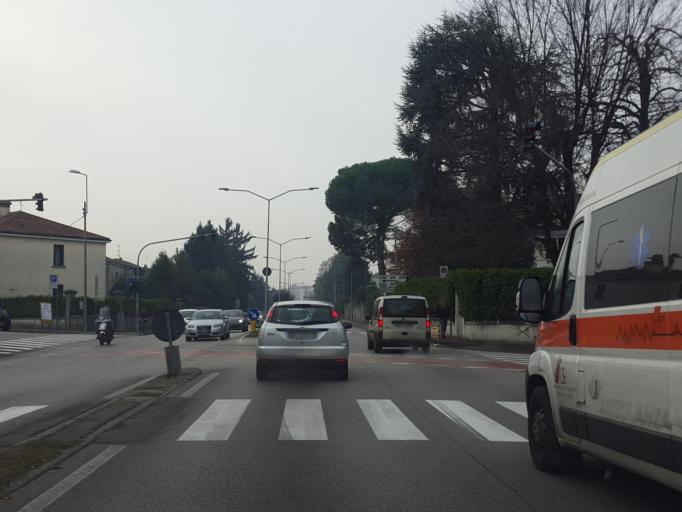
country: IT
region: Veneto
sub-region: Provincia di Vicenza
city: Vicenza
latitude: 45.5575
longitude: 11.5423
